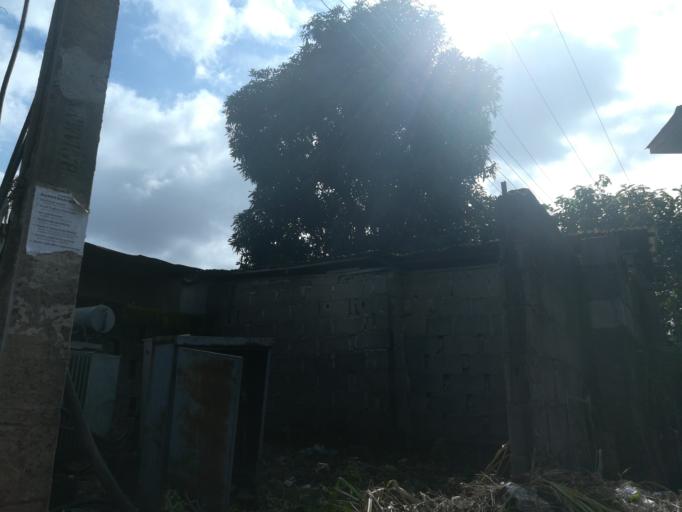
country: NG
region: Lagos
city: Somolu
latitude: 6.5476
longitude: 3.3725
